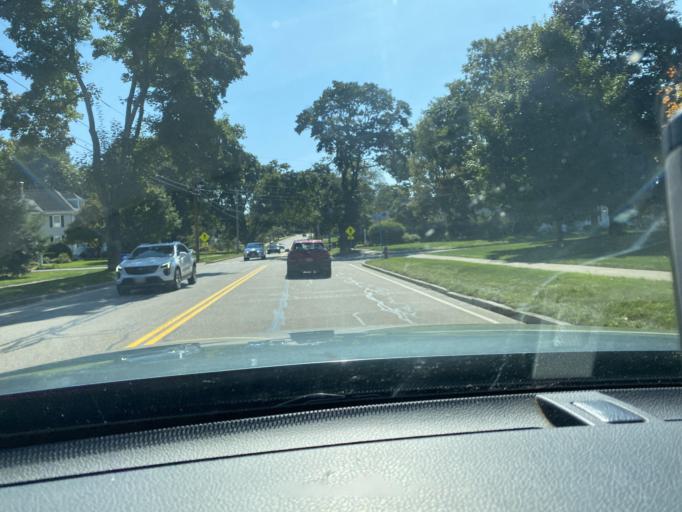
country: US
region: Massachusetts
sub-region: Norfolk County
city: Walpole
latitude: 42.1421
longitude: -71.2516
